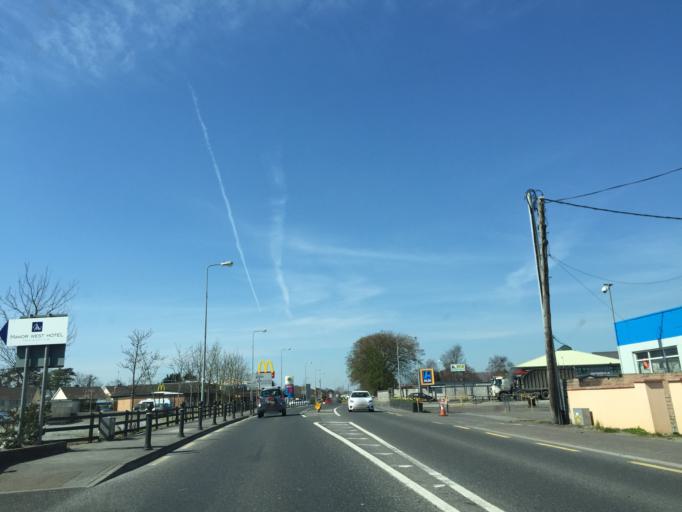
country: IE
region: Munster
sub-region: Ciarrai
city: Tralee
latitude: 52.2647
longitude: -9.6764
